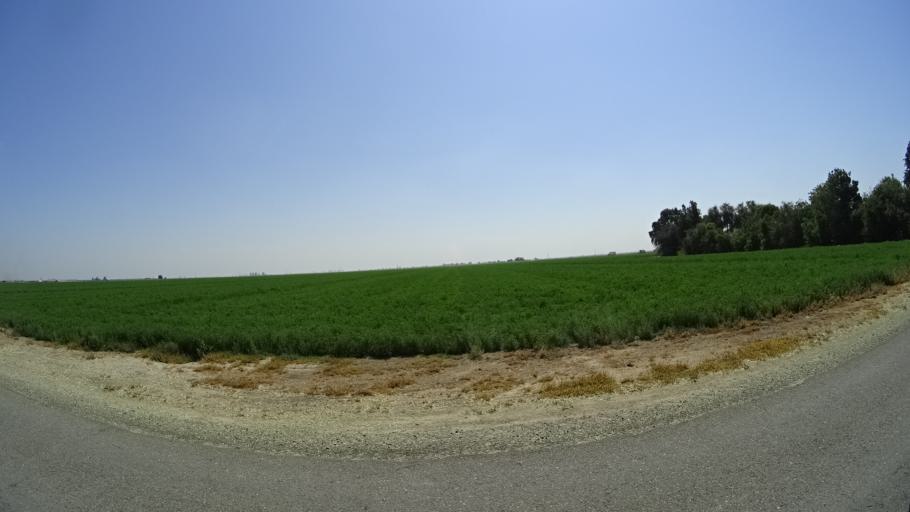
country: US
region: California
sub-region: Tulare County
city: Goshen
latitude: 36.3882
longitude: -119.5289
